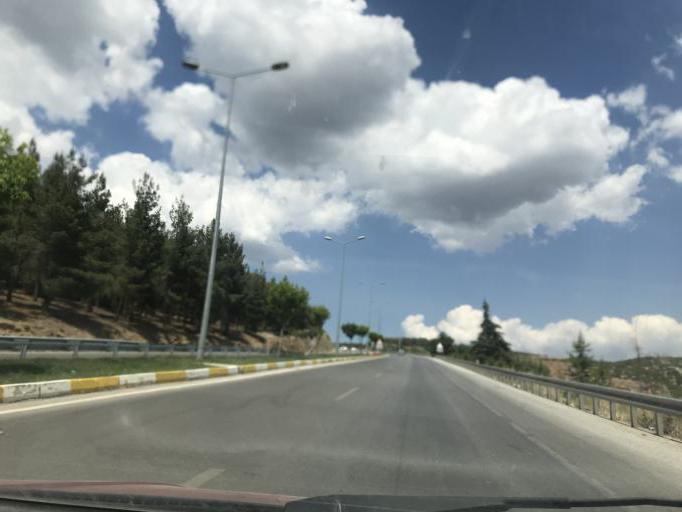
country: TR
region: Denizli
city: Tavas
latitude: 37.5746
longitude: 29.0849
